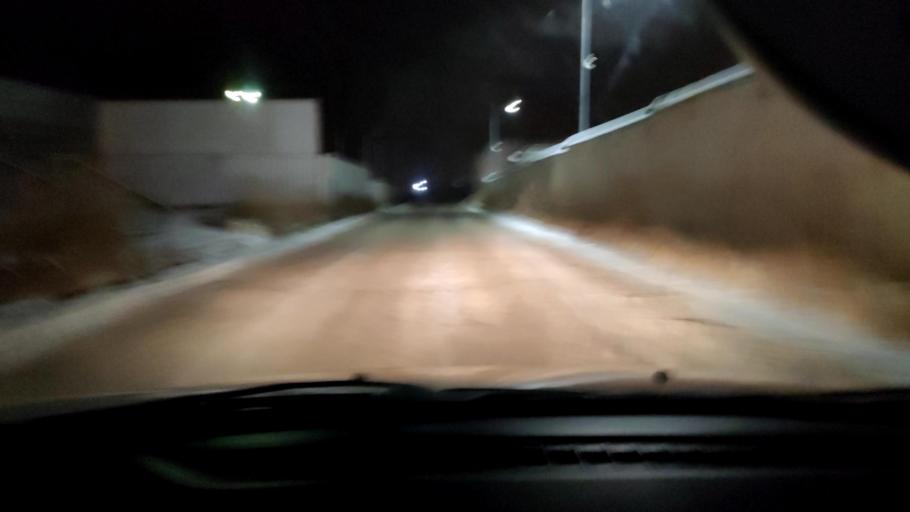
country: RU
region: Perm
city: Kondratovo
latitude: 57.9448
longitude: 56.0716
